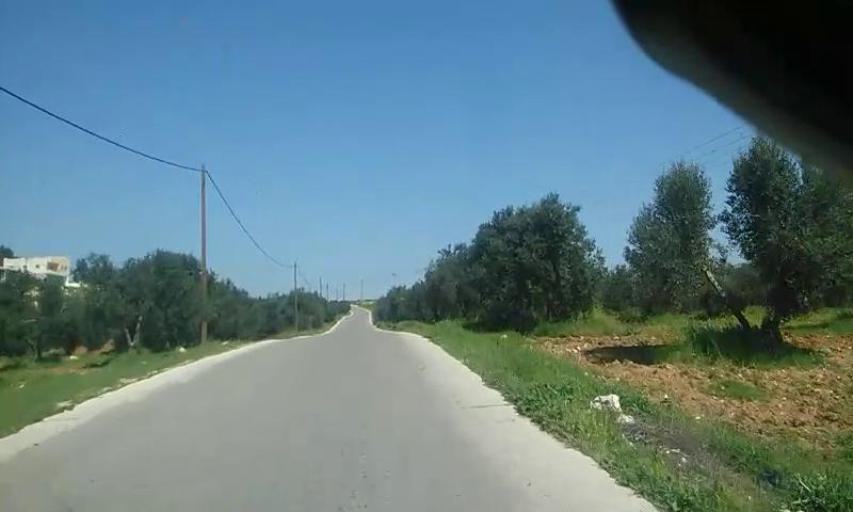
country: PS
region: West Bank
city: Al Majd
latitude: 31.4720
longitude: 34.9477
